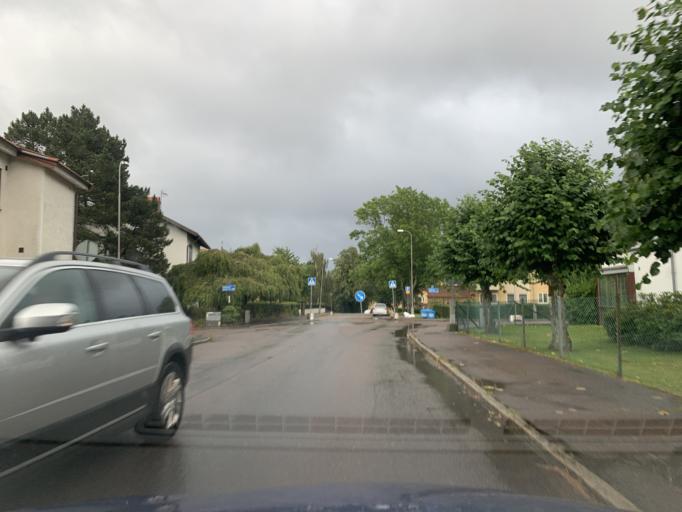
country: SE
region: Vaestra Goetaland
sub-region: Goteborg
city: Goeteborg
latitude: 57.7018
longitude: 12.0089
